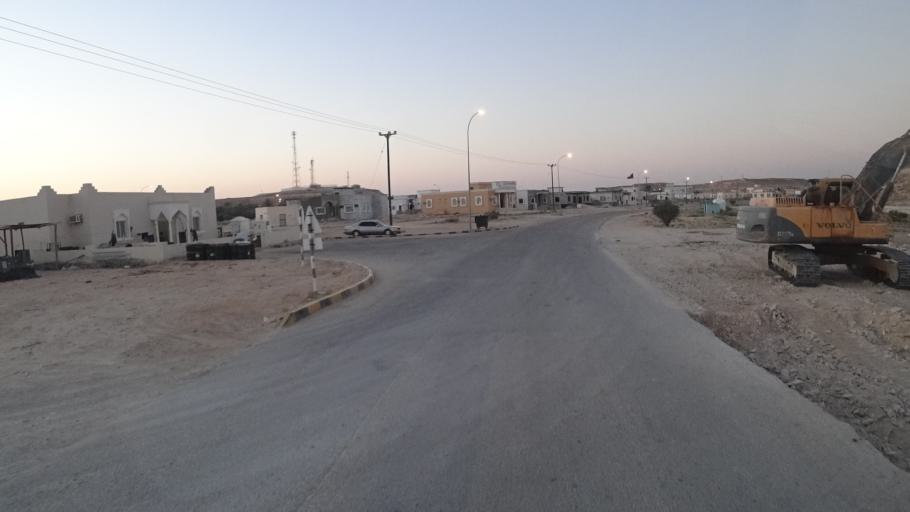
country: OM
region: Zufar
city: Salalah
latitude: 17.4827
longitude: 53.3494
